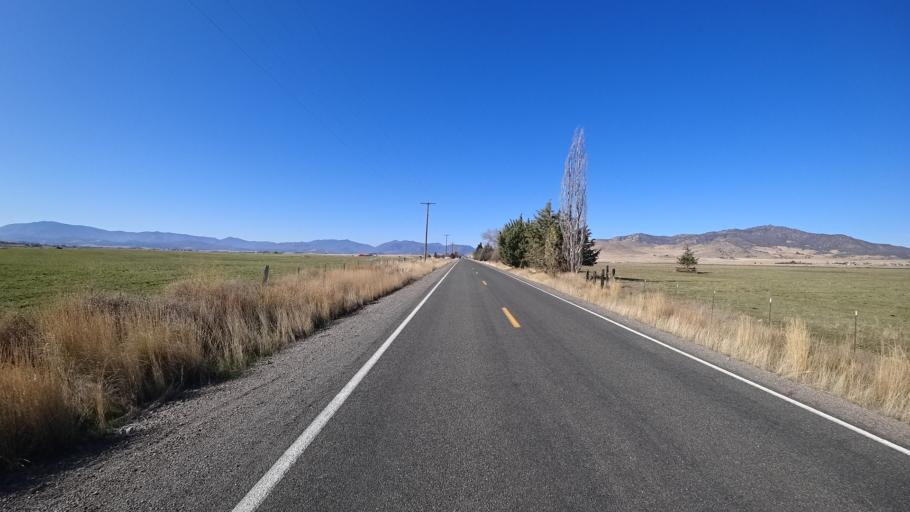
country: US
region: California
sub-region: Siskiyou County
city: Montague
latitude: 41.7706
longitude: -122.4871
